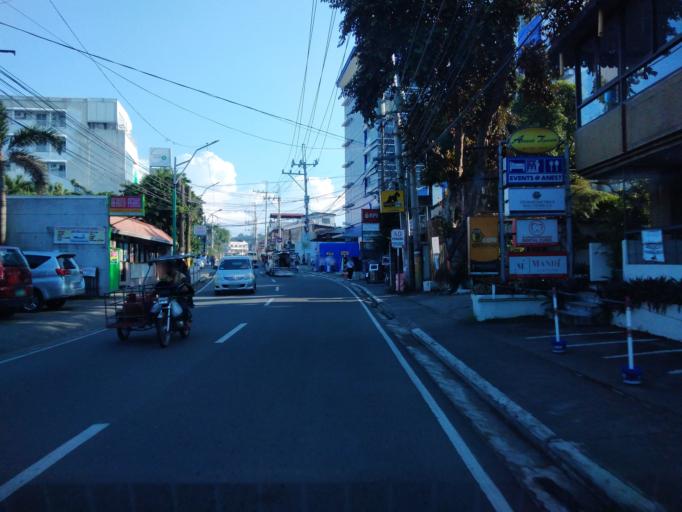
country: PH
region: Calabarzon
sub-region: Province of Laguna
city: Los Banos
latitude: 14.1714
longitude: 121.2433
